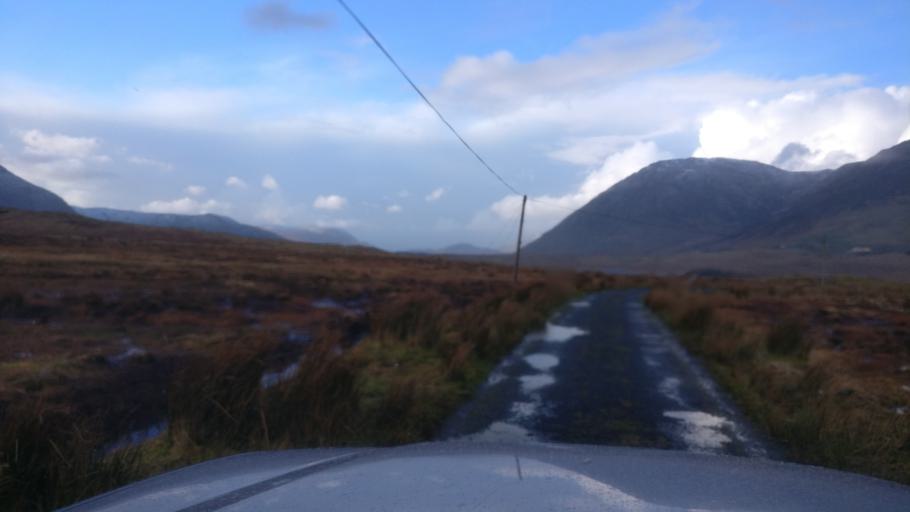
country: IE
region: Connaught
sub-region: County Galway
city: Clifden
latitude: 53.4973
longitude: -9.7056
